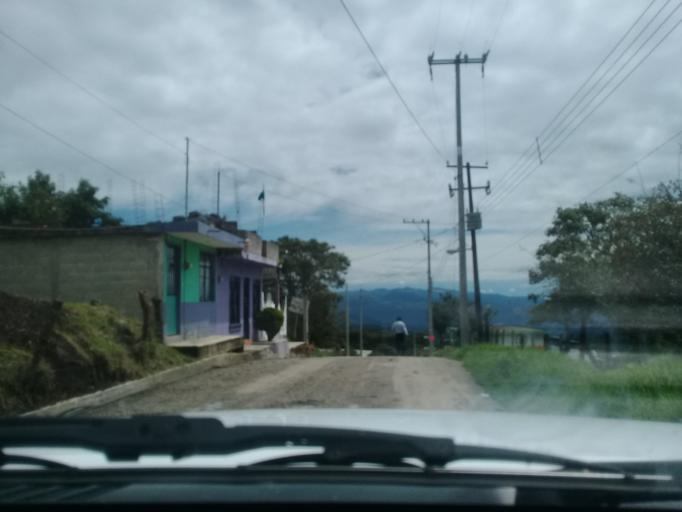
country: MX
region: Veracruz
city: Rafael Lucio
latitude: 19.5938
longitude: -96.9845
